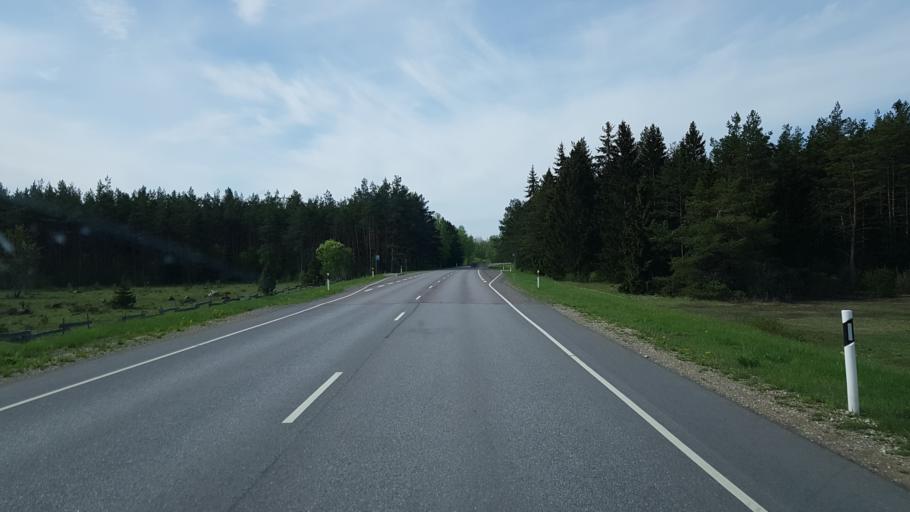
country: EE
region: Saare
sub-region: Kuressaare linn
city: Kuressaare
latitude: 58.3749
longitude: 22.7314
